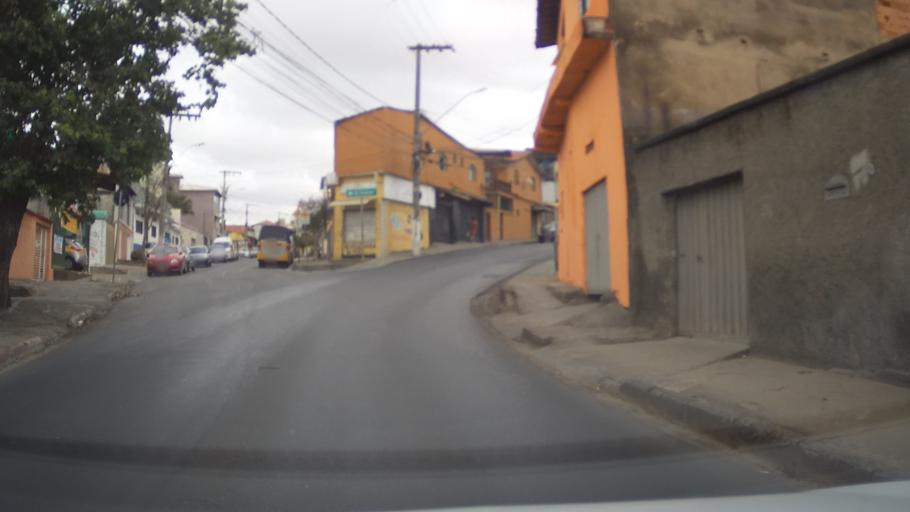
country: BR
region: Minas Gerais
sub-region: Belo Horizonte
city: Belo Horizonte
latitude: -19.8439
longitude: -43.9467
